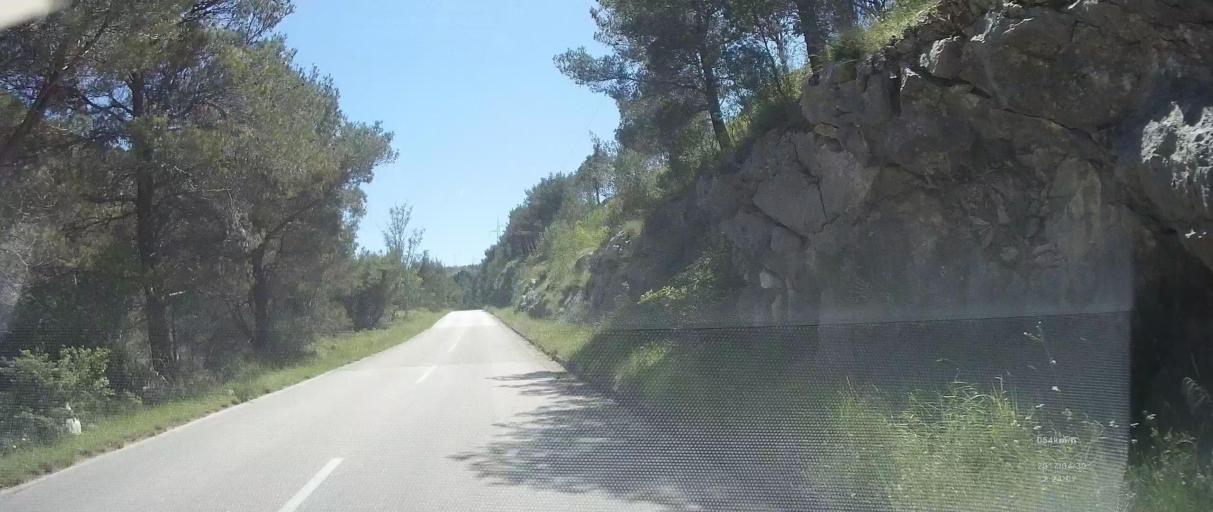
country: HR
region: Splitsko-Dalmatinska
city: Zrnovnica
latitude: 43.5135
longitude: 16.5833
